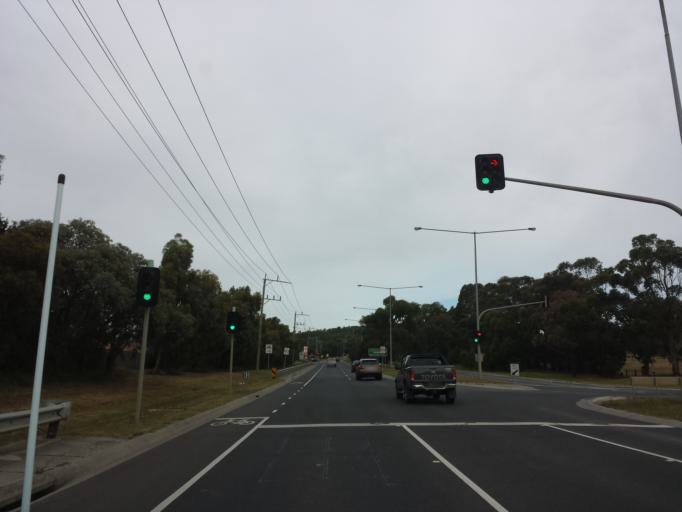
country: AU
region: Victoria
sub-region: Knox
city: Rowville
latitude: -37.9284
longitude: 145.2618
